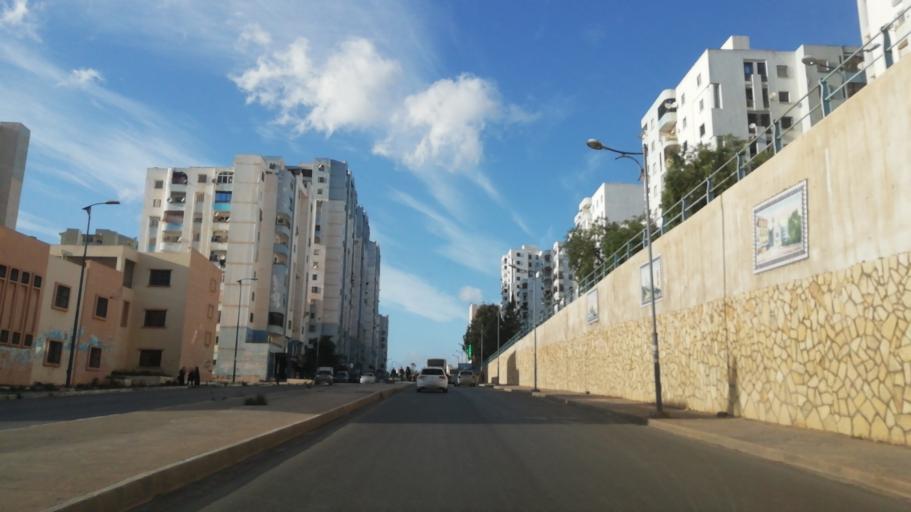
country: DZ
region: Oran
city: Bir el Djir
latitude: 35.7000
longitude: -0.5746
